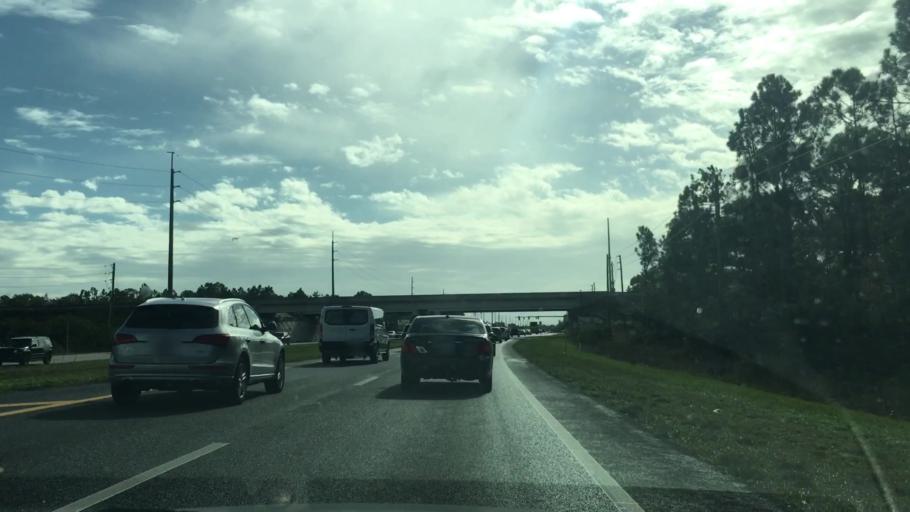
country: US
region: Florida
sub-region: Osceola County
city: Celebration
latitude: 28.3524
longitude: -81.4927
